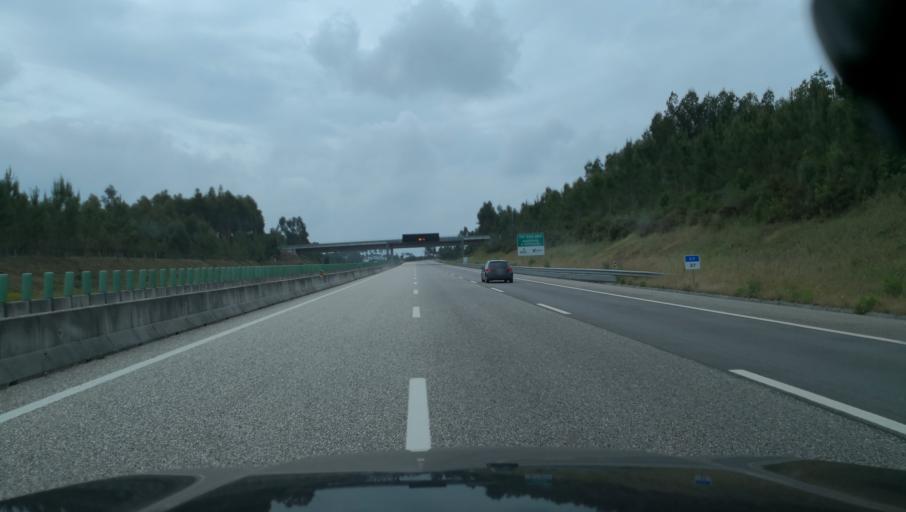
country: PT
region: Coimbra
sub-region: Figueira da Foz
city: Lavos
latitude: 40.0294
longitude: -8.8135
